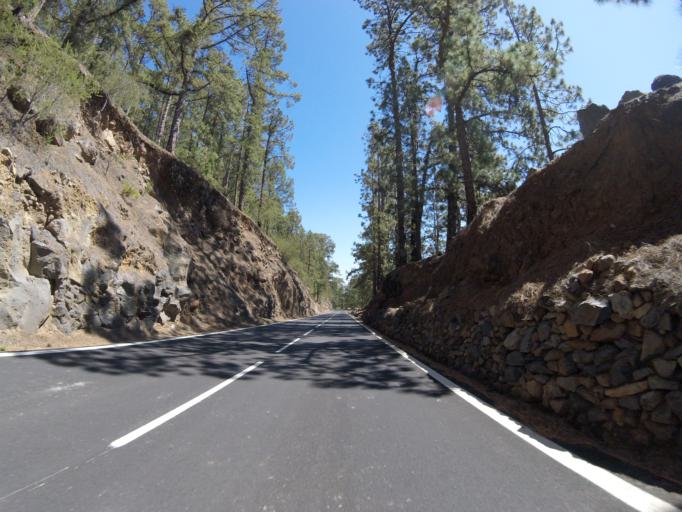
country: ES
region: Canary Islands
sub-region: Provincia de Santa Cruz de Tenerife
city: Vilaflor
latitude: 28.1703
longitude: -16.6363
